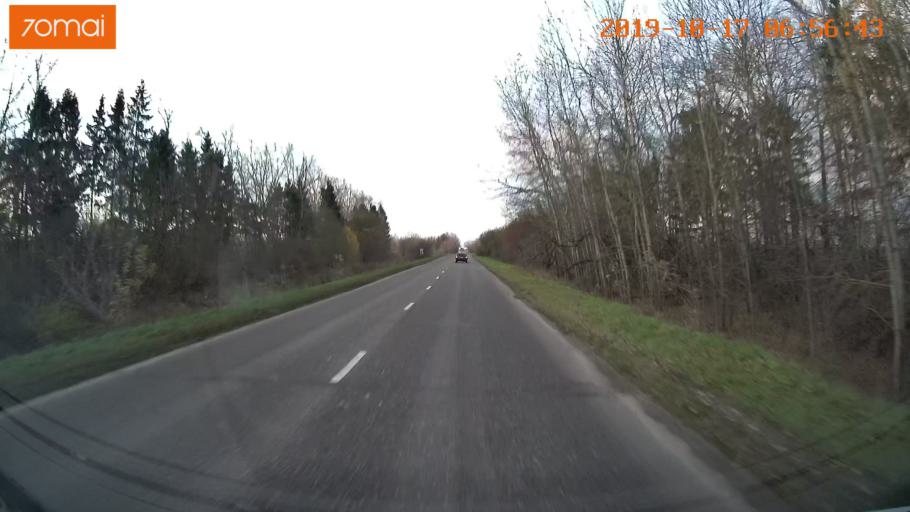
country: RU
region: Vladimir
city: Suzdal'
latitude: 56.4434
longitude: 40.4451
